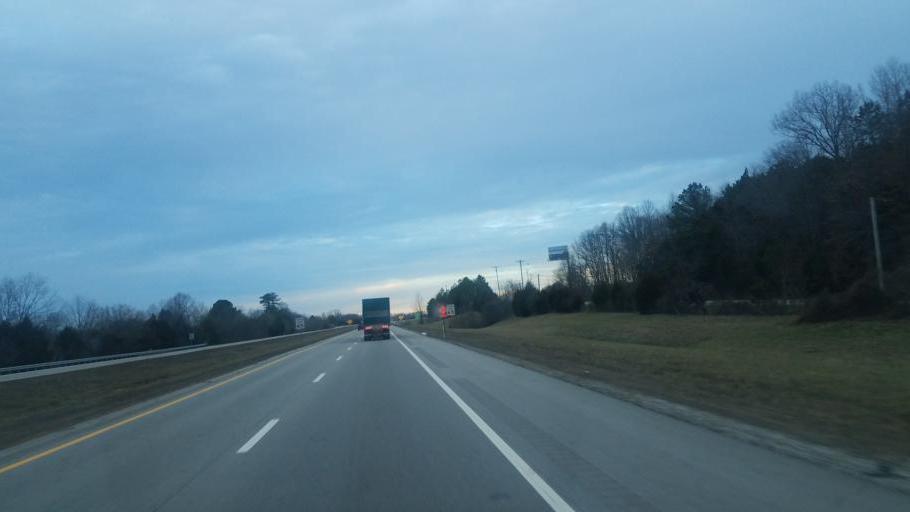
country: US
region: Tennessee
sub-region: Putnam County
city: Cookeville
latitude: 36.0924
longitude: -85.5053
